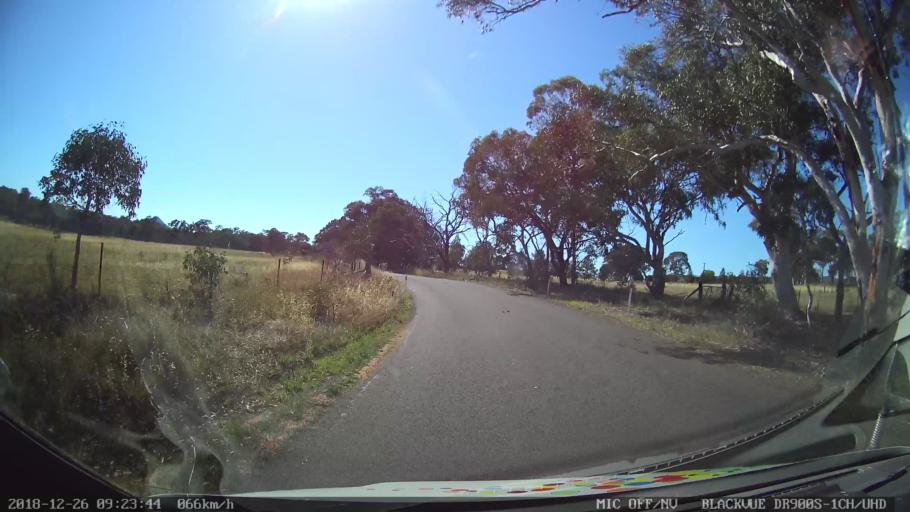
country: AU
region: New South Wales
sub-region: Mid-Western Regional
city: Kandos
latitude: -32.8080
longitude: 149.9904
